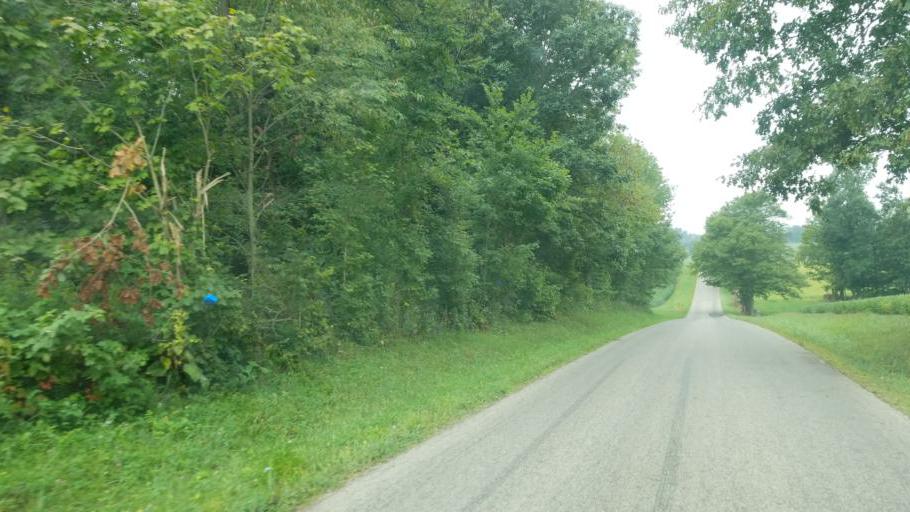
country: US
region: Ohio
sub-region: Licking County
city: Utica
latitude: 40.2482
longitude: -82.3698
